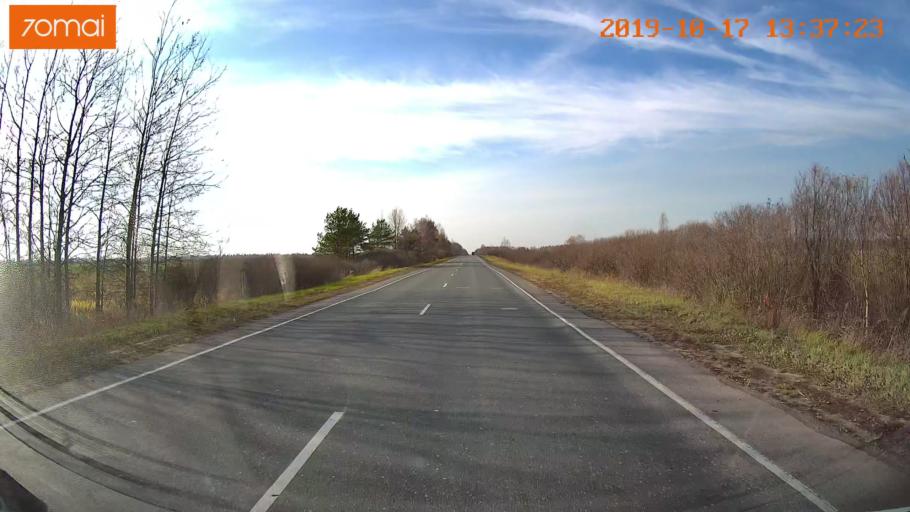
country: RU
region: Rjazan
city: Tuma
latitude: 55.1415
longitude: 40.6404
